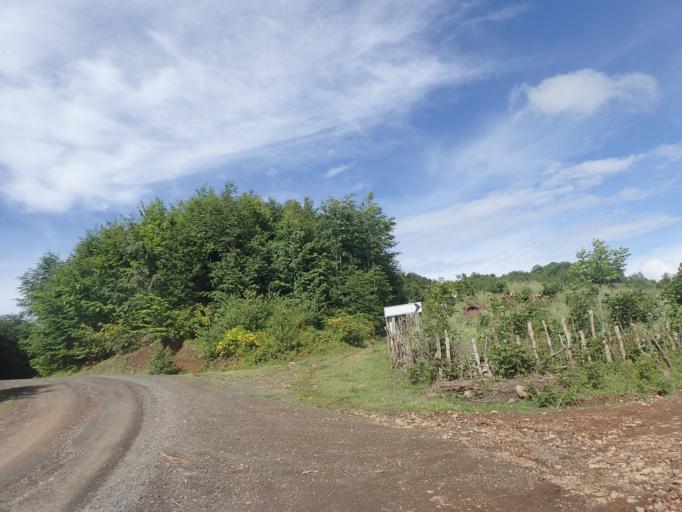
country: TR
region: Samsun
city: Salipazari
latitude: 40.9431
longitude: 36.8708
